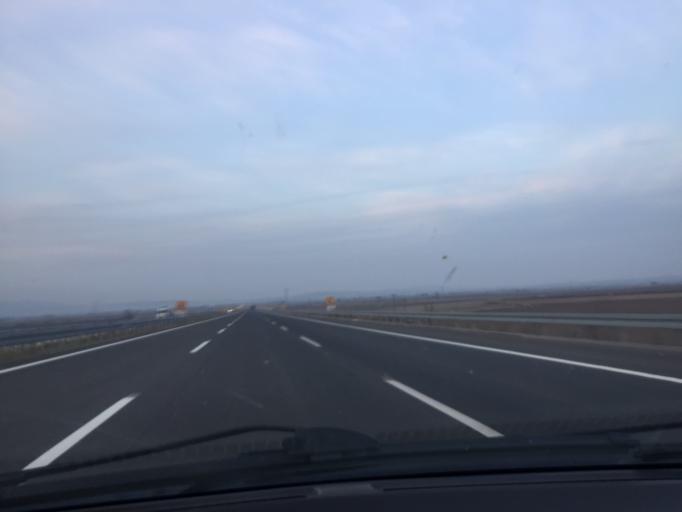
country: TR
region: Manisa
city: Halitpasa
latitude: 38.7092
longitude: 27.6468
